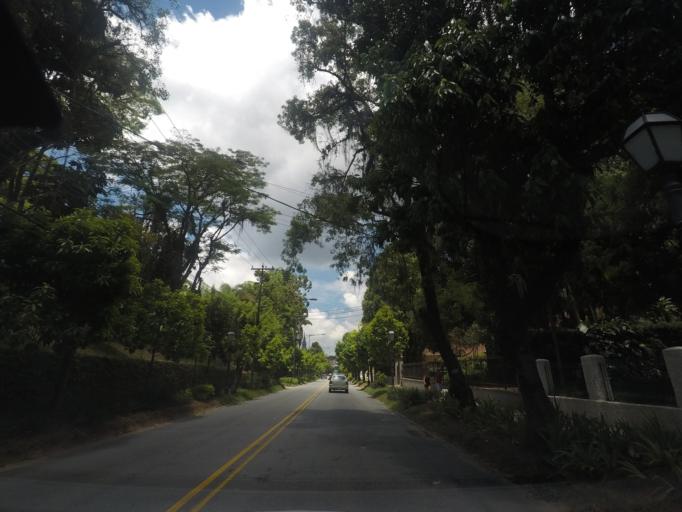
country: BR
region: Rio de Janeiro
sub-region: Petropolis
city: Petropolis
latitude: -22.5036
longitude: -43.1739
